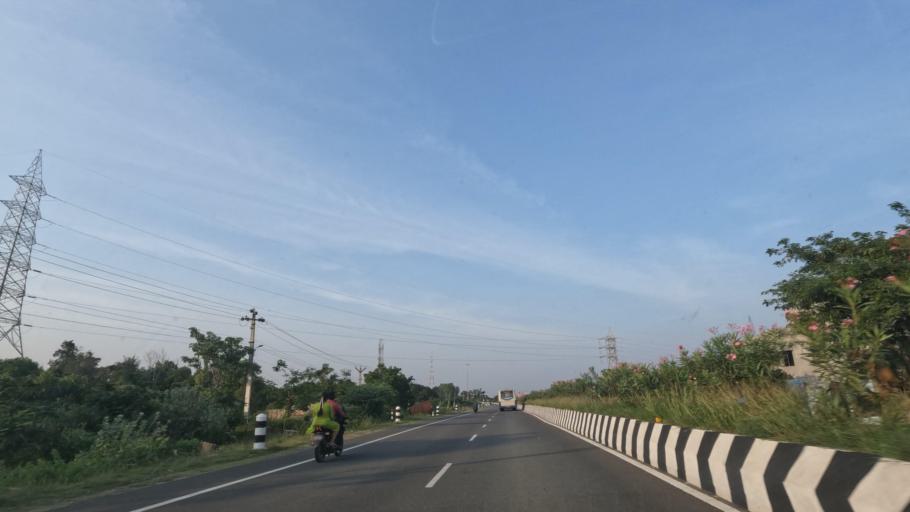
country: IN
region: Tamil Nadu
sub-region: Kancheepuram
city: Mamallapuram
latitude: 12.7019
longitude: 80.2225
